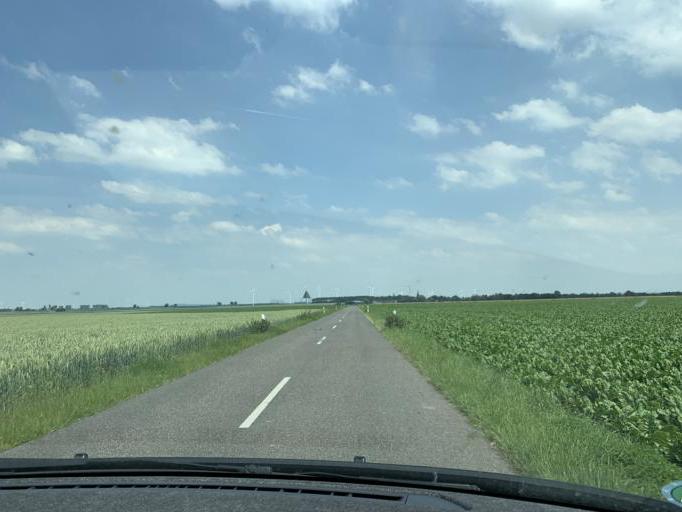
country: DE
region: North Rhine-Westphalia
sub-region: Regierungsbezirk Koln
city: Titz
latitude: 50.9619
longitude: 6.4361
